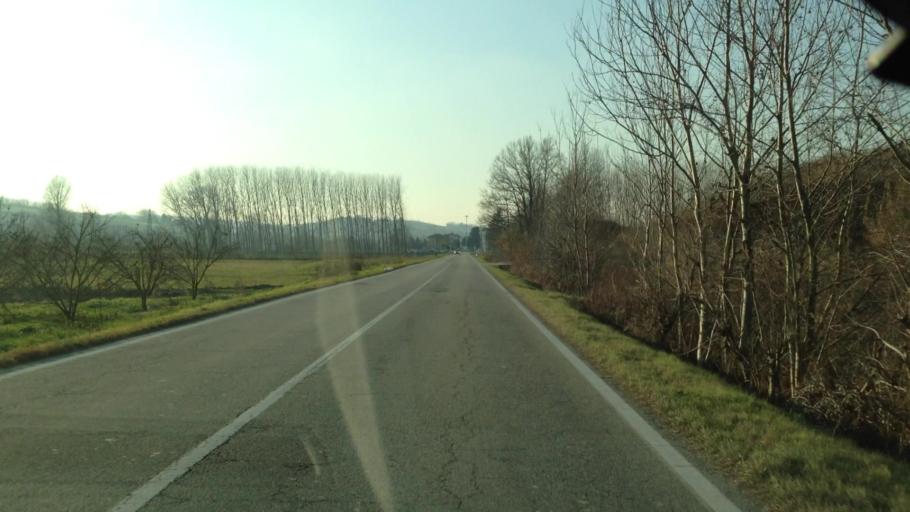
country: IT
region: Piedmont
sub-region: Provincia di Asti
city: Montaldo Scarampi
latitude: 44.8167
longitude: 8.2627
